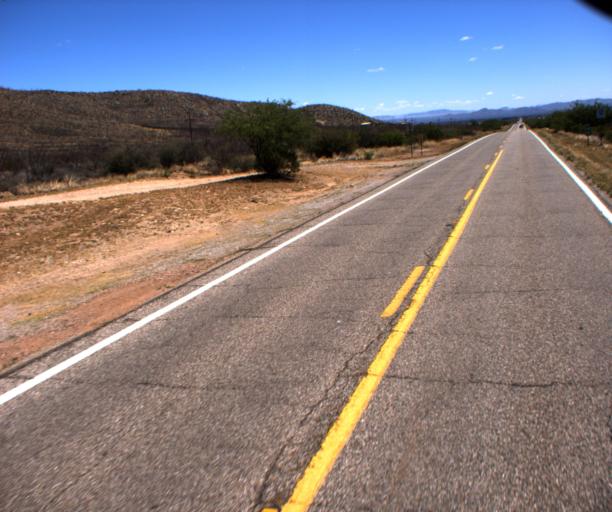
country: US
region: Arizona
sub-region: Cochise County
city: Huachuca City
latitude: 31.6918
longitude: -110.3948
